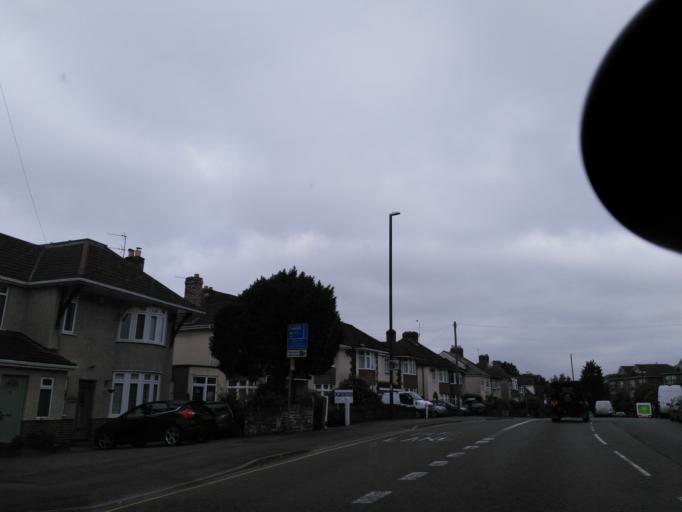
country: GB
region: England
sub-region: Bath and North East Somerset
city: Whitchurch
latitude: 51.4347
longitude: -2.5534
